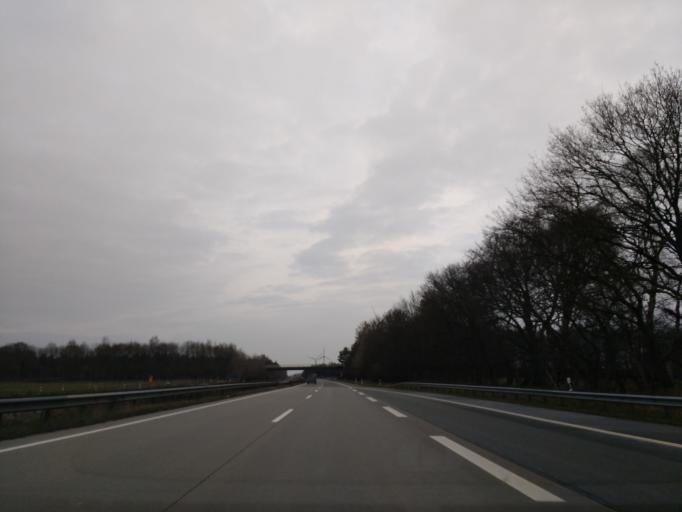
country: DE
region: Lower Saxony
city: Langen
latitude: 53.6225
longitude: 8.6651
